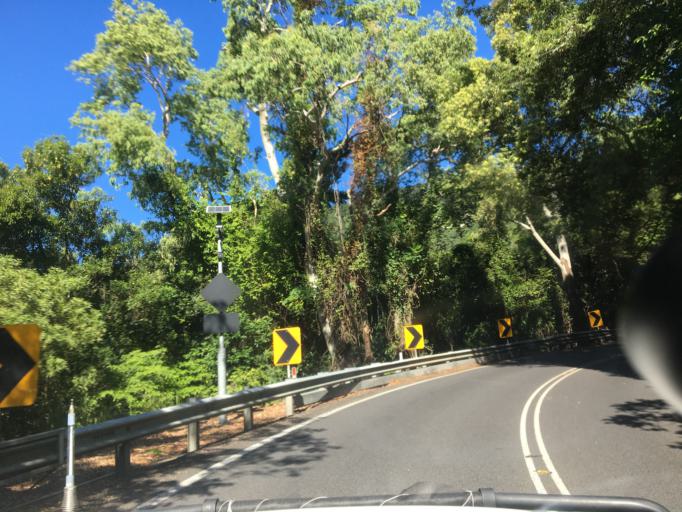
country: AU
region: Queensland
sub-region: Cairns
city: Redlynch
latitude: -16.8408
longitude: 145.6832
